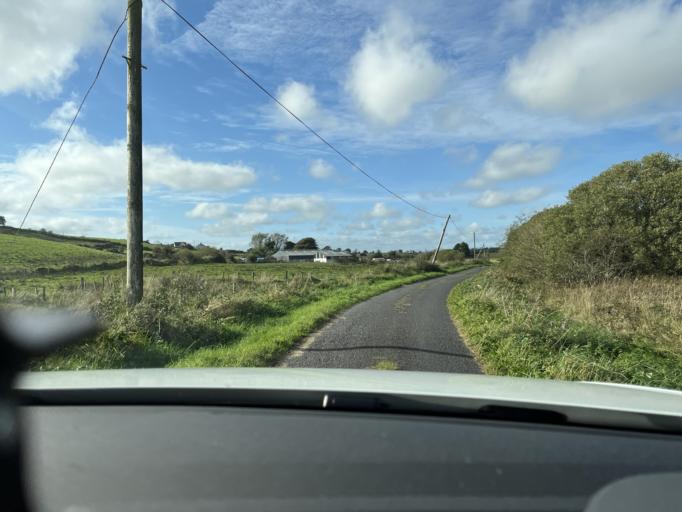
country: IE
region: Connaught
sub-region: Sligo
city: Ballymote
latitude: 54.0715
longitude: -8.4284
